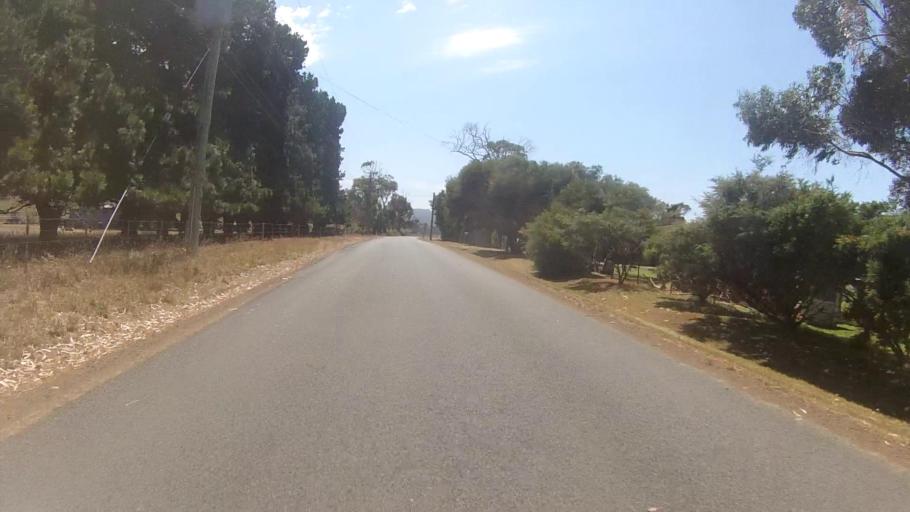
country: AU
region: Tasmania
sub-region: Sorell
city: Sorell
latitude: -42.8255
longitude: 147.8596
